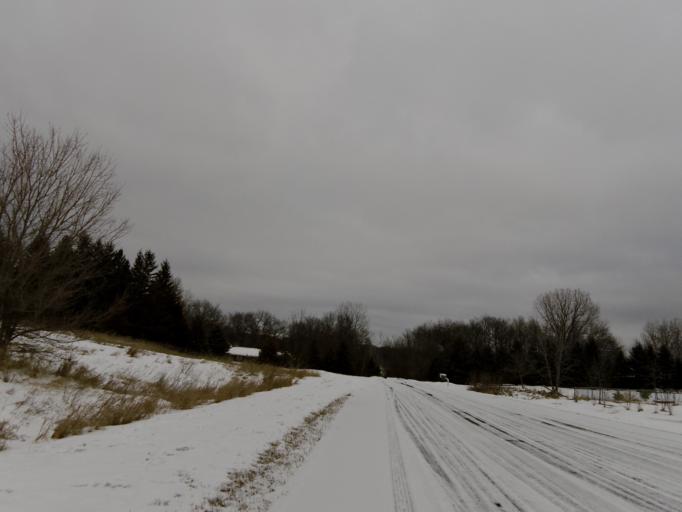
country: US
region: Minnesota
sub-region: Washington County
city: Lake Elmo
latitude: 44.9555
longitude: -92.8487
